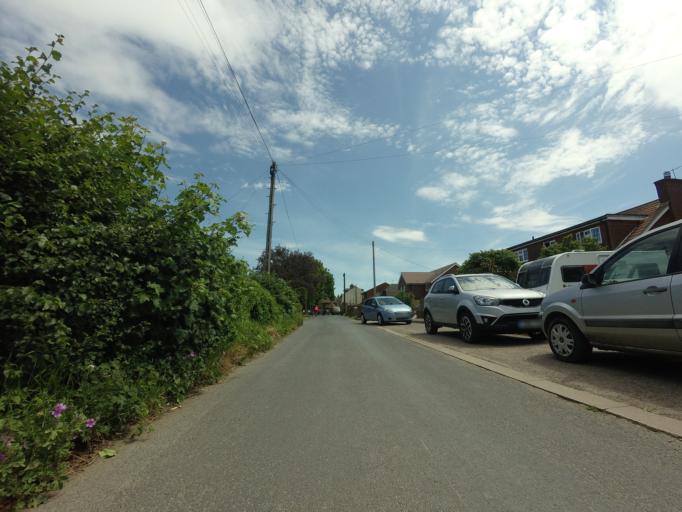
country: GB
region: England
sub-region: Kent
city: Cliffe
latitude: 51.4613
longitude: 0.4958
